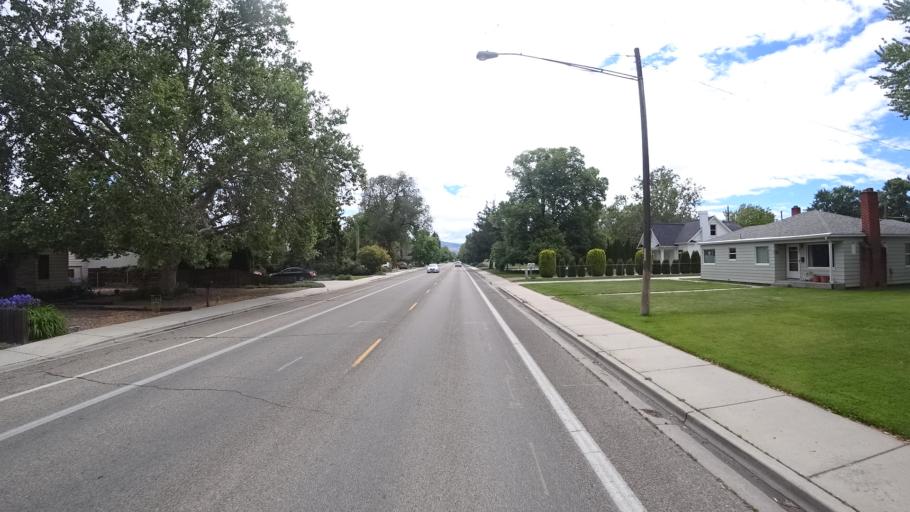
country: US
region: Idaho
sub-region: Ada County
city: Boise
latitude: 43.5789
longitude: -116.1899
